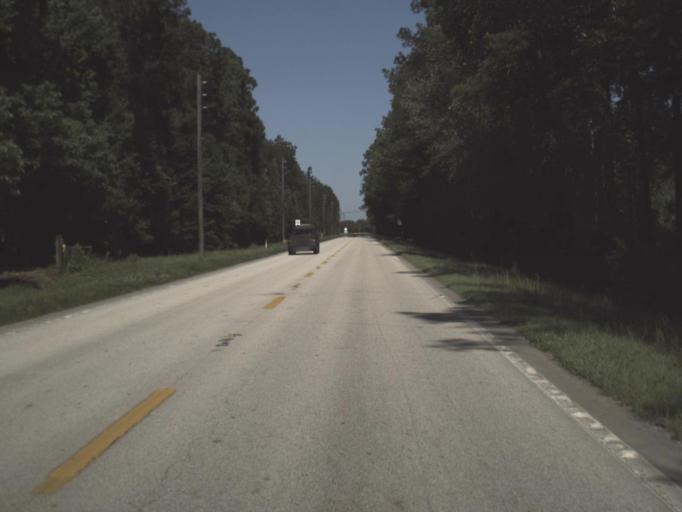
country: US
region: Florida
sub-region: Duval County
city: Baldwin
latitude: 30.3029
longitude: -81.9624
